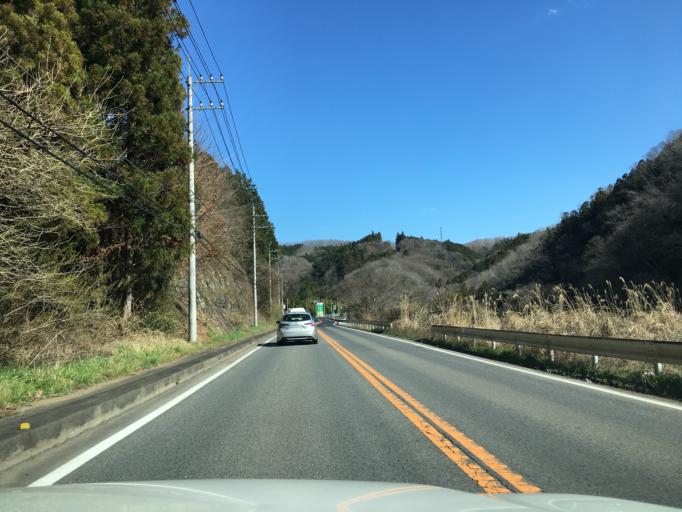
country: JP
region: Tochigi
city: Motegi
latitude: 36.5476
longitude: 140.2277
